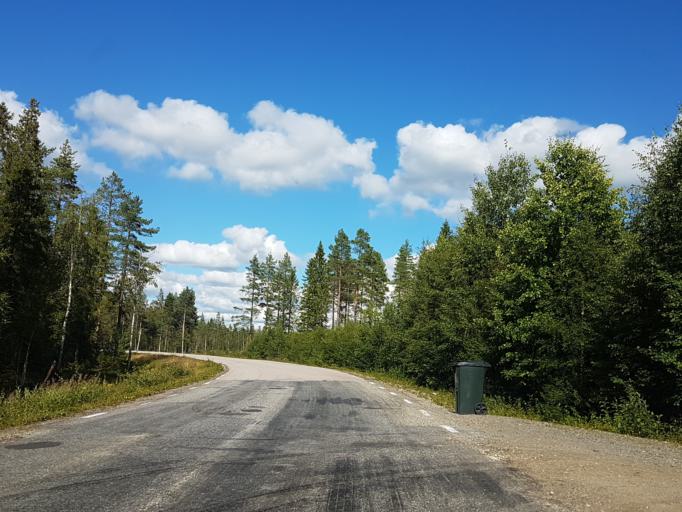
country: SE
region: Vaesterbotten
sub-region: Skelleftea Kommun
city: Burtraesk
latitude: 64.2401
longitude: 20.4831
